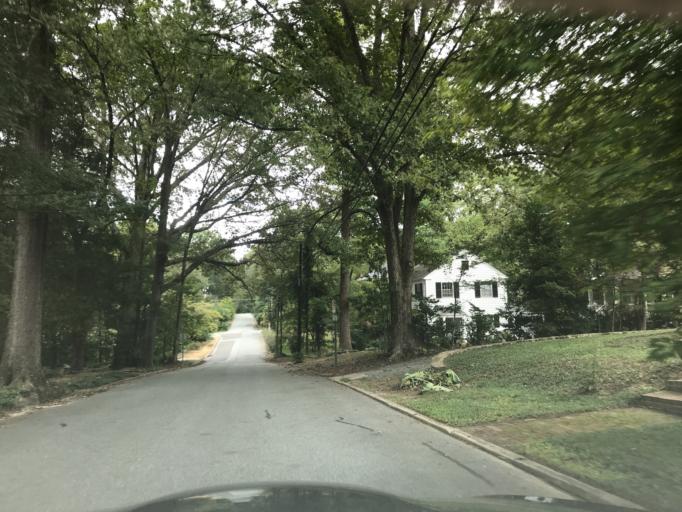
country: US
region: North Carolina
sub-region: Orange County
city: Chapel Hill
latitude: 35.9185
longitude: -79.0483
